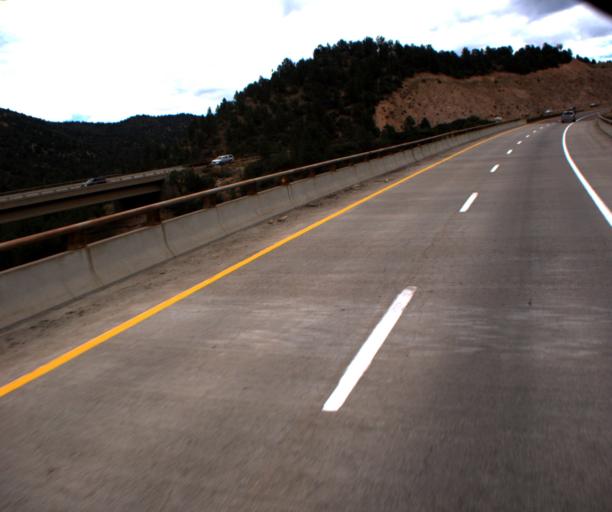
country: US
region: Arizona
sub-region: Gila County
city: Star Valley
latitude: 34.2778
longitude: -111.1692
